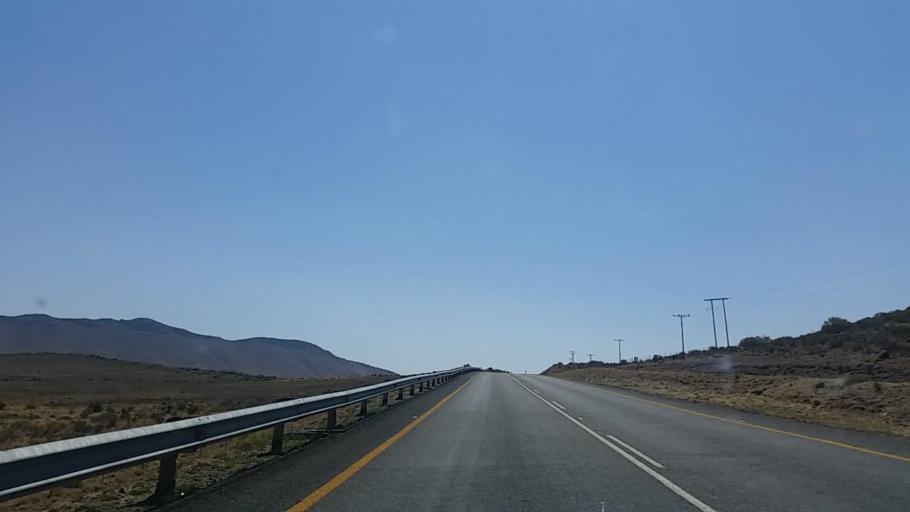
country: ZA
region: Eastern Cape
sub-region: Chris Hani District Municipality
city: Middelburg
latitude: -31.7738
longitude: 24.9088
